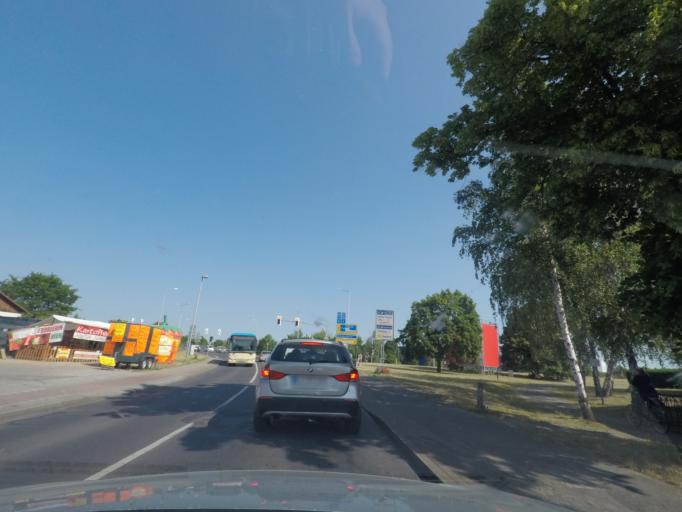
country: DE
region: Brandenburg
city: Schulzendorf
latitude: 52.3647
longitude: 13.5558
